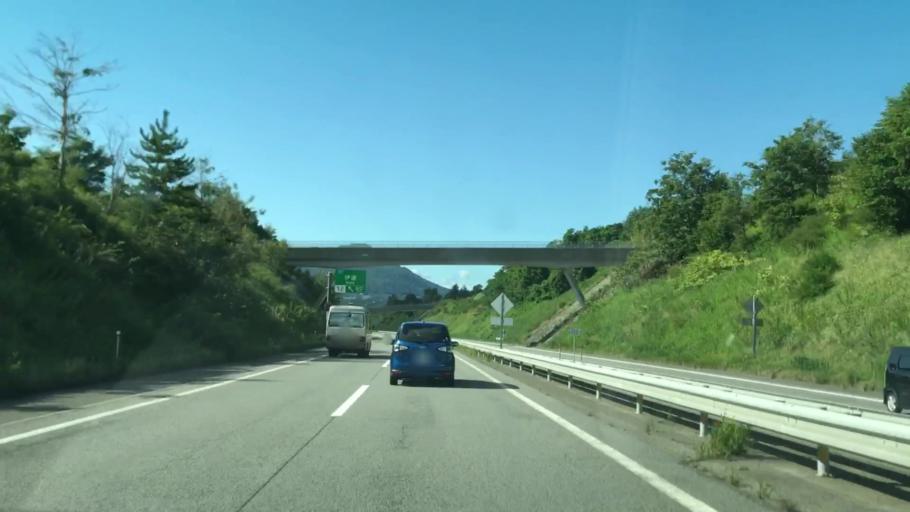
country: JP
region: Hokkaido
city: Date
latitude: 42.4780
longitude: 140.9007
